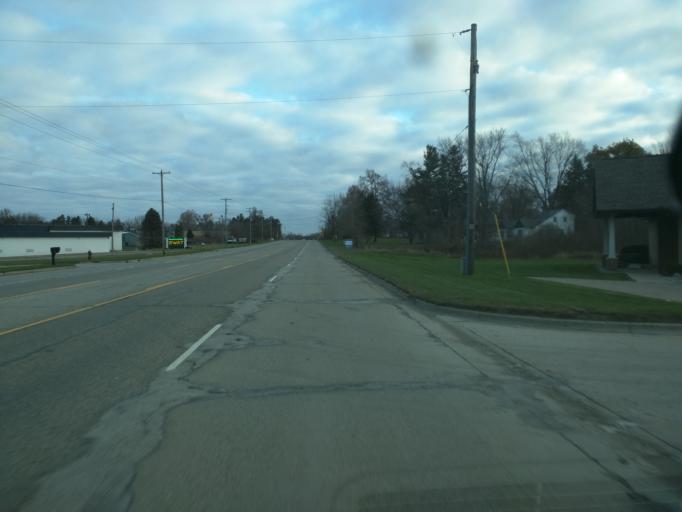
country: US
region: Michigan
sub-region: Eaton County
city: Dimondale
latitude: 42.6574
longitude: -84.5979
